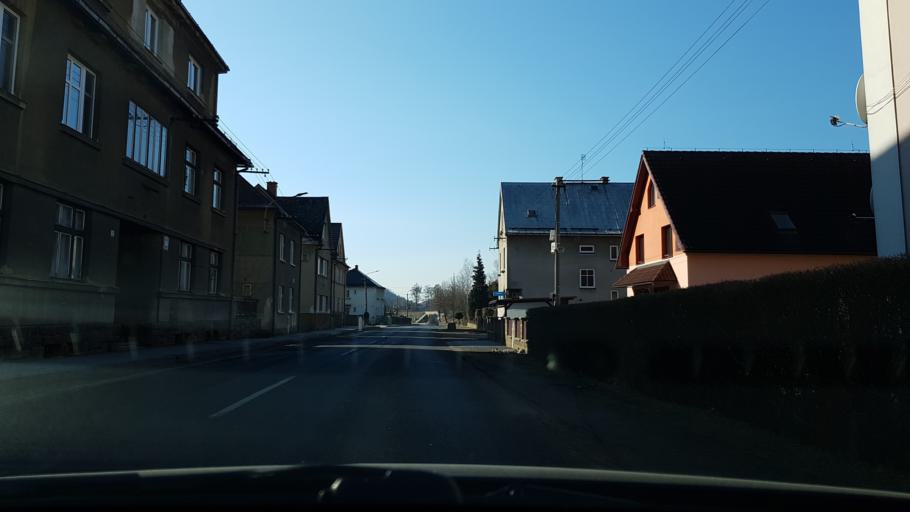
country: CZ
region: Olomoucky
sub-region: Okres Sumperk
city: Hanusovice
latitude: 50.0711
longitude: 16.9314
